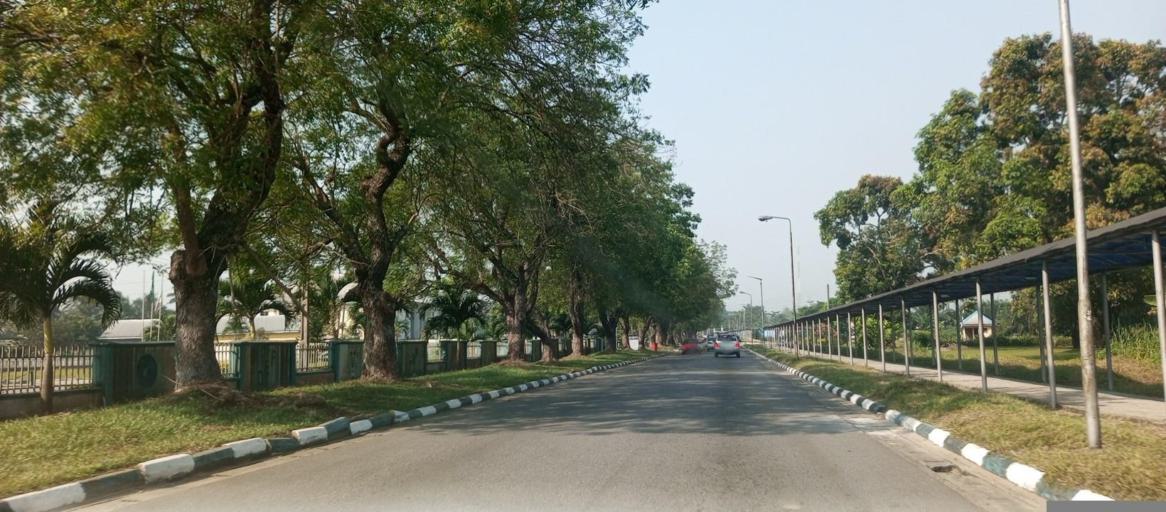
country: NG
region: Rivers
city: Emuoha
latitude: 4.9026
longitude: 6.9101
